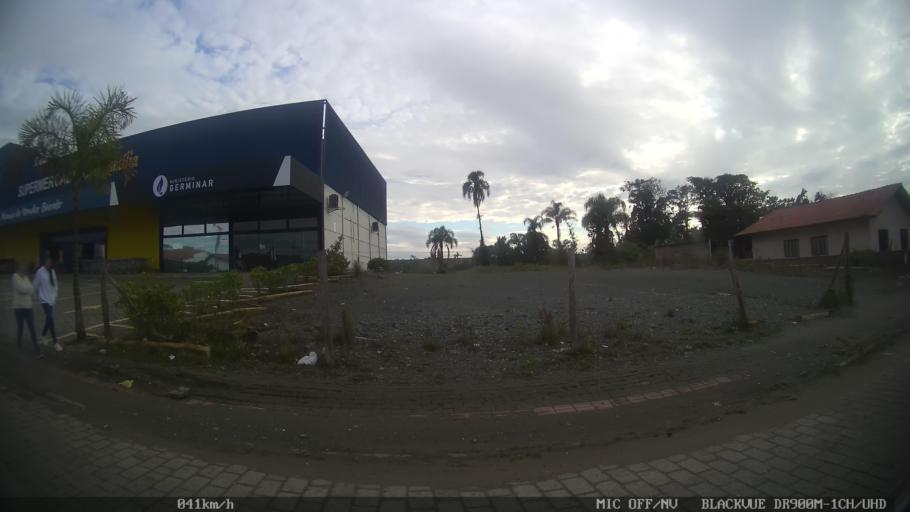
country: BR
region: Santa Catarina
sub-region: Barra Velha
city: Barra Velha
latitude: -26.6292
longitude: -48.6937
